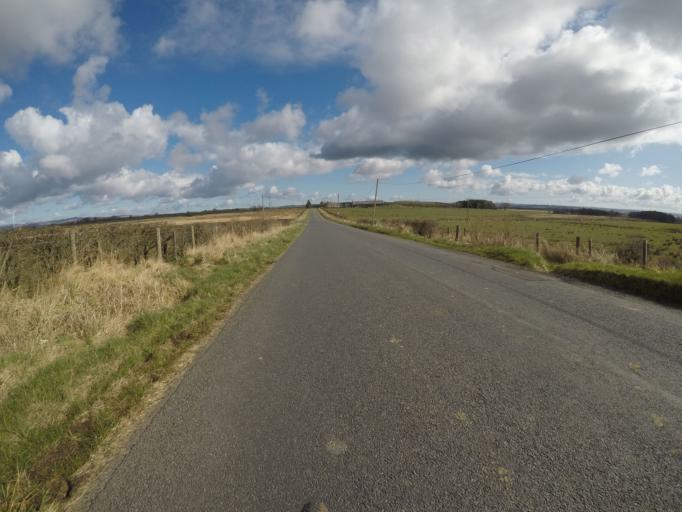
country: GB
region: Scotland
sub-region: North Ayrshire
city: Kilwinning
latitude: 55.6844
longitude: -4.6494
